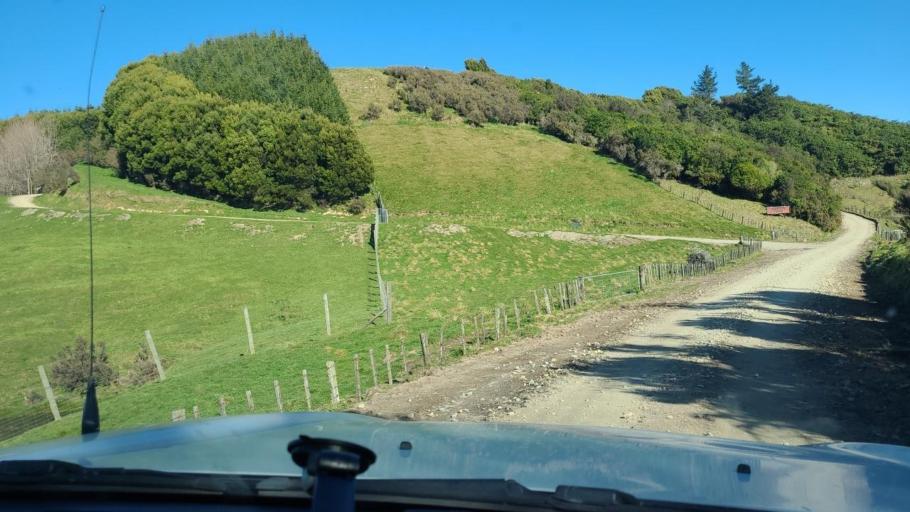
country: NZ
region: Hawke's Bay
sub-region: Wairoa District
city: Wairoa
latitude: -38.6827
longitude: 177.4618
